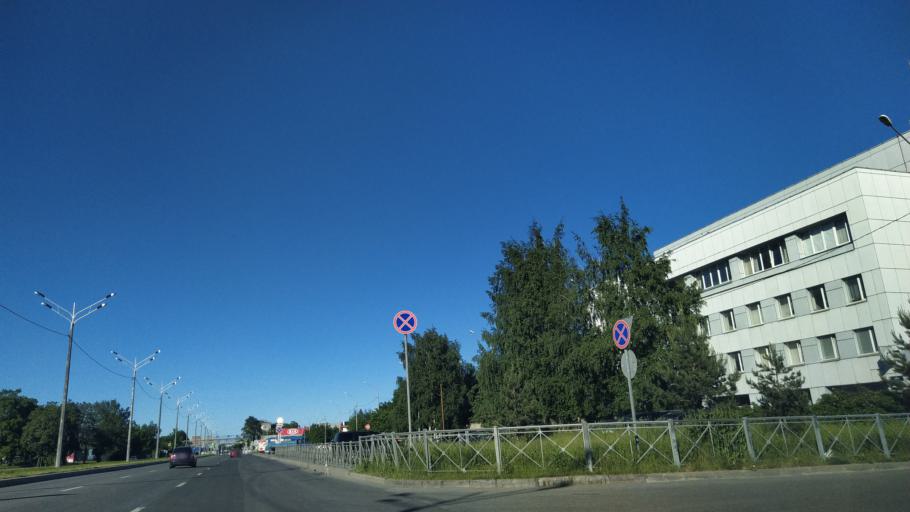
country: RU
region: St.-Petersburg
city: Kupchino
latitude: 59.8871
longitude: 30.3754
